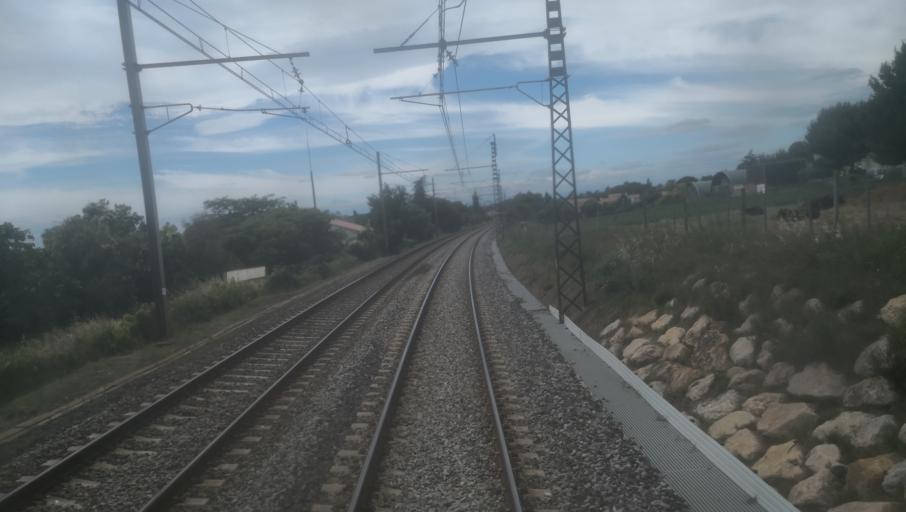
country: FR
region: Languedoc-Roussillon
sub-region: Departement de l'Herault
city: Cers
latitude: 43.3228
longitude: 3.3111
